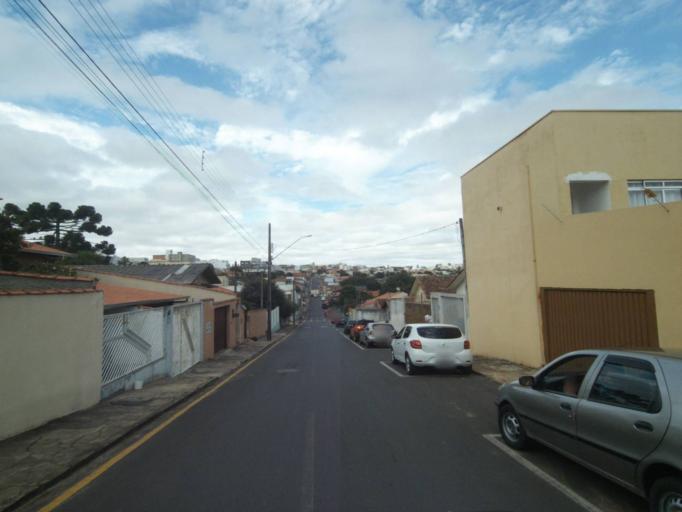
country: BR
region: Parana
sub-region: Telemaco Borba
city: Telemaco Borba
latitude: -24.3235
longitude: -50.6228
